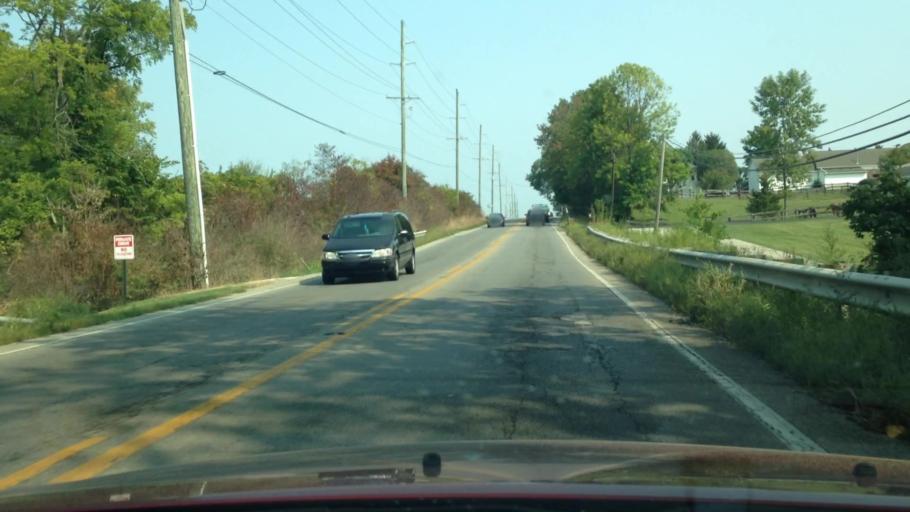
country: US
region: Indiana
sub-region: Johnson County
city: Waterloo
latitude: 39.5676
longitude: -86.1589
